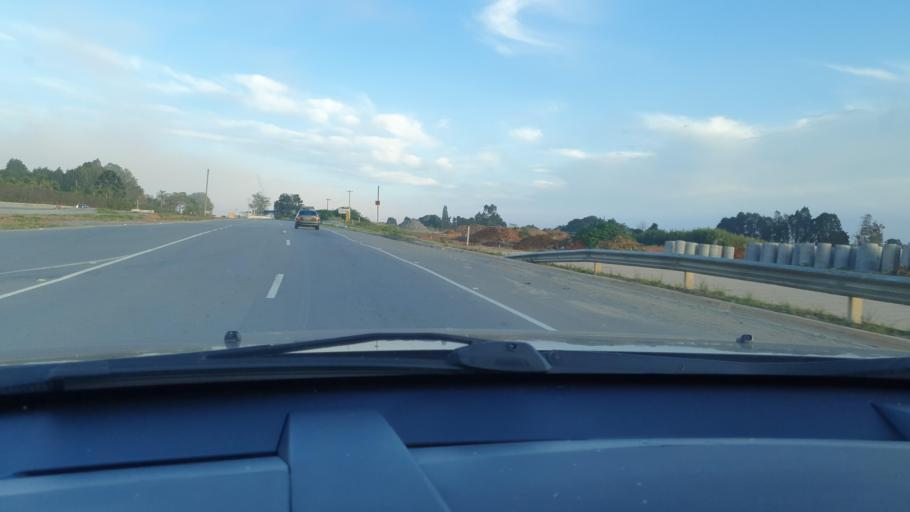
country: BR
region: Sao Paulo
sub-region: Ibiuna
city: Ibiuna
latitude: -23.6481
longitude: -47.1395
